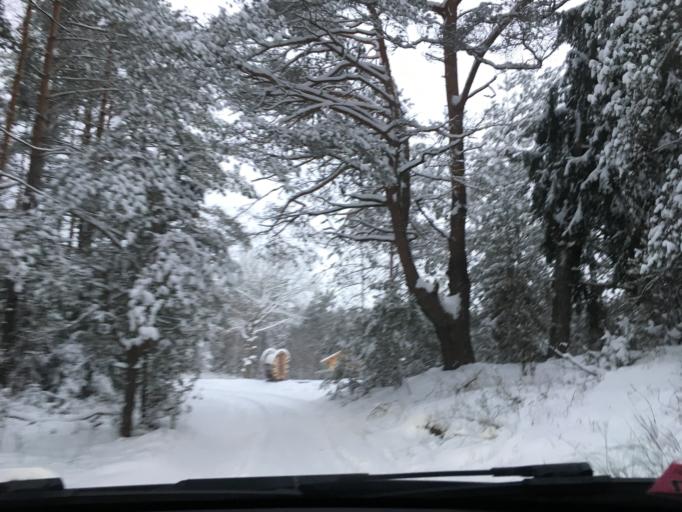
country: LT
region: Alytaus apskritis
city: Druskininkai
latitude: 53.9221
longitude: 24.1889
